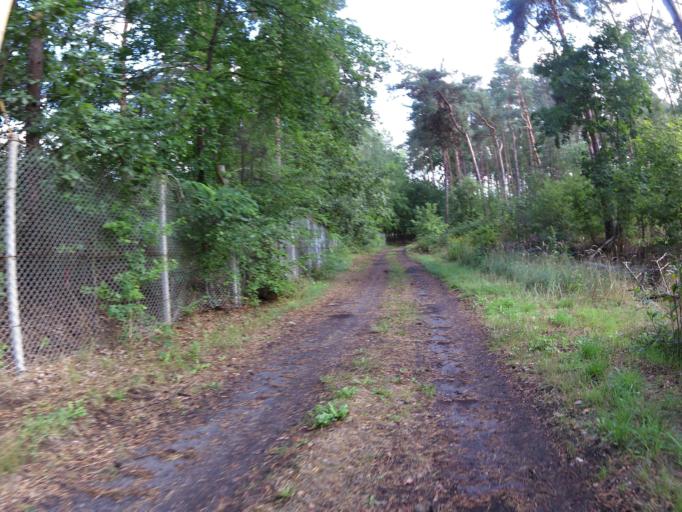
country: DE
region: Brandenburg
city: Storkow
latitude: 52.2649
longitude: 13.9494
